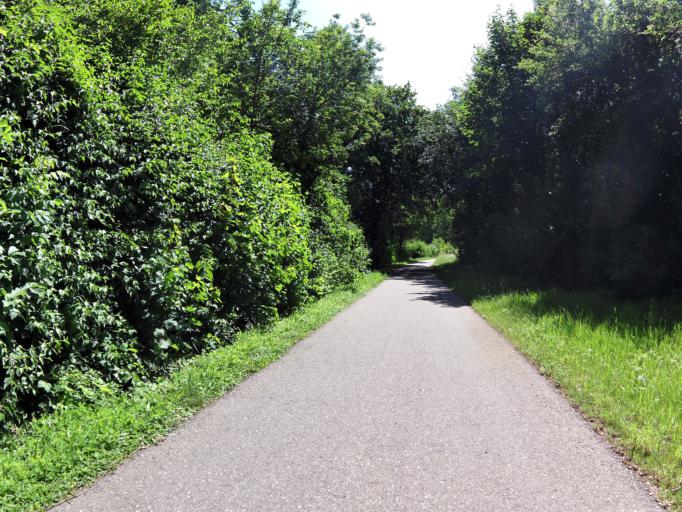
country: DE
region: Baden-Wuerttemberg
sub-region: Freiburg Region
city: Hohberg
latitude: 48.3337
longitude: 7.9146
